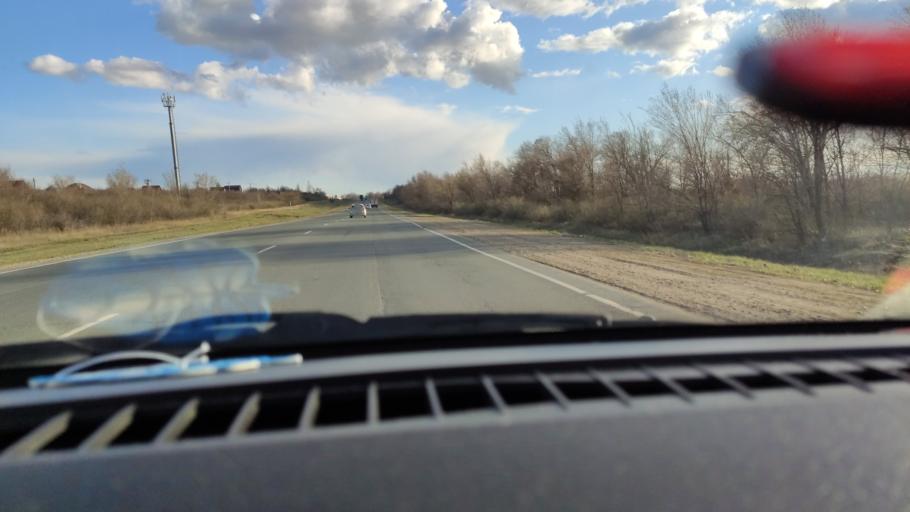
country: RU
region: Saratov
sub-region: Saratovskiy Rayon
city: Saratov
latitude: 51.6834
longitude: 46.0024
